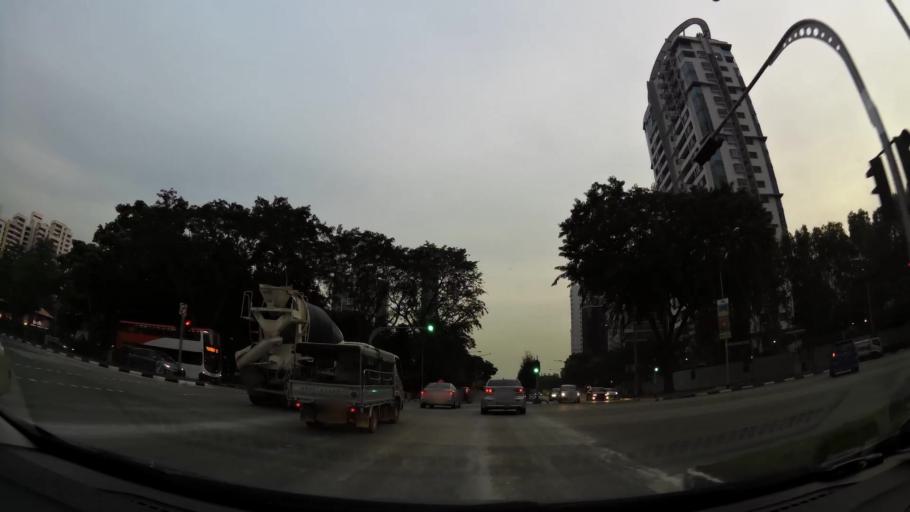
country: SG
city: Singapore
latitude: 1.3011
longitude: 103.8856
